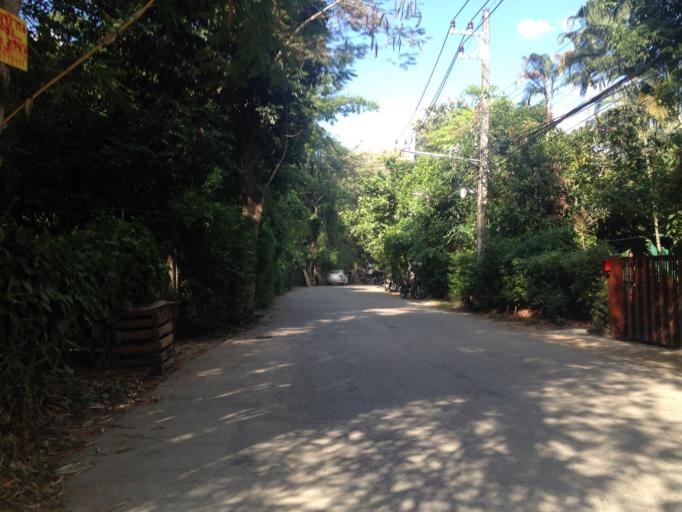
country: TH
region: Chiang Mai
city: Chiang Mai
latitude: 18.7734
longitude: 98.9462
